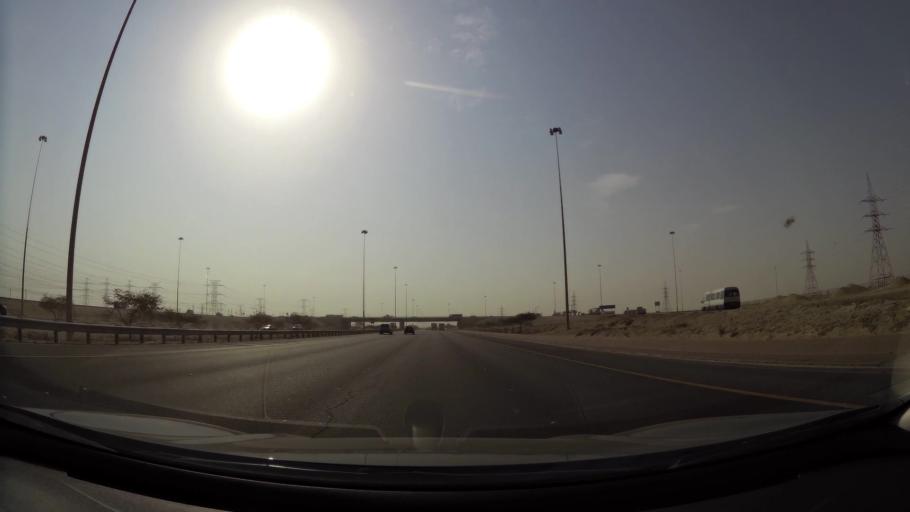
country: KW
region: Al Ahmadi
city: Al Ahmadi
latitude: 28.9936
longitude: 48.1006
